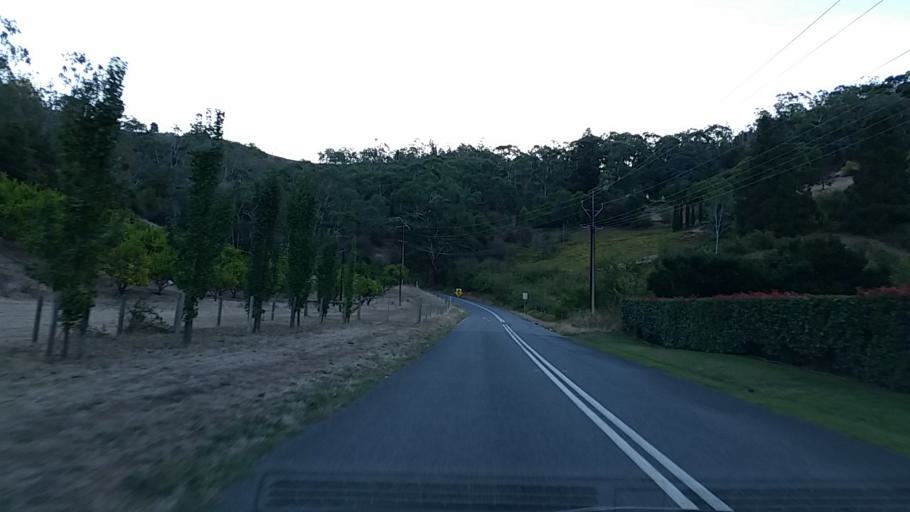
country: AU
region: South Australia
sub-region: Adelaide Hills
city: Adelaide Hills
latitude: -34.8838
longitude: 138.7501
